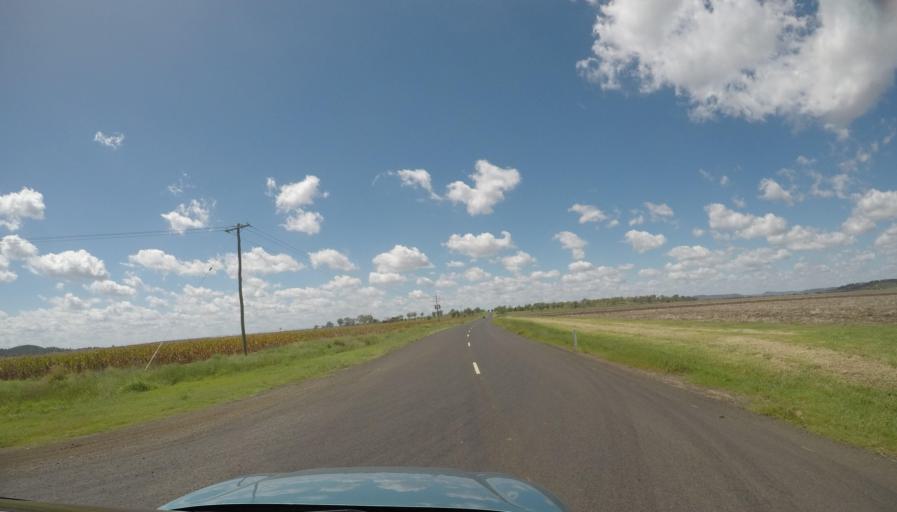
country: AU
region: Queensland
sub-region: Toowoomba
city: Oakey
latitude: -27.5272
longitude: 151.5777
